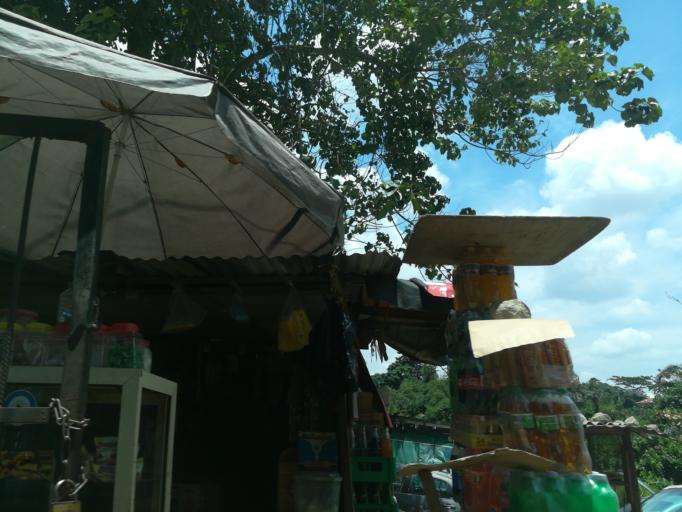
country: NG
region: Lagos
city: Ebute Ikorodu
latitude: 6.6041
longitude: 3.4948
